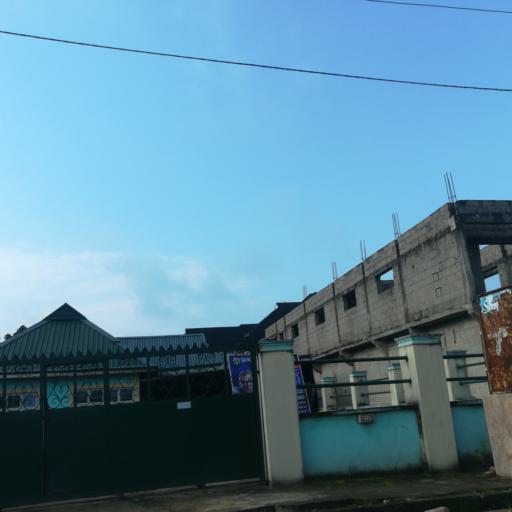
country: NG
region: Rivers
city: Port Harcourt
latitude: 4.8490
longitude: 6.9602
